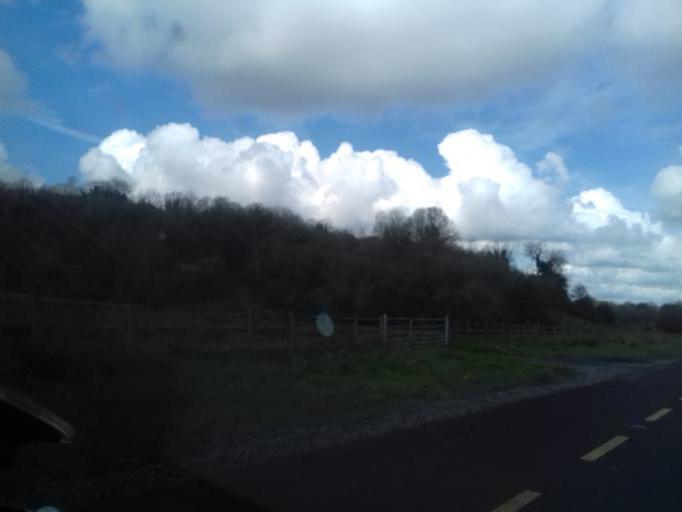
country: IE
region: Ulster
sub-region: An Cabhan
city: Belturbet
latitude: 54.0706
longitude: -7.4095
